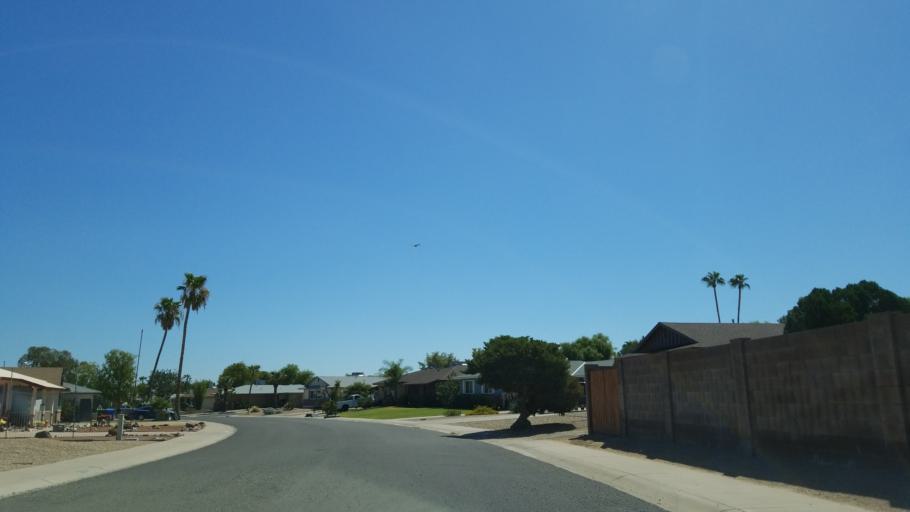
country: US
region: Arizona
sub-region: Maricopa County
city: Paradise Valley
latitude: 33.5938
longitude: -112.0338
